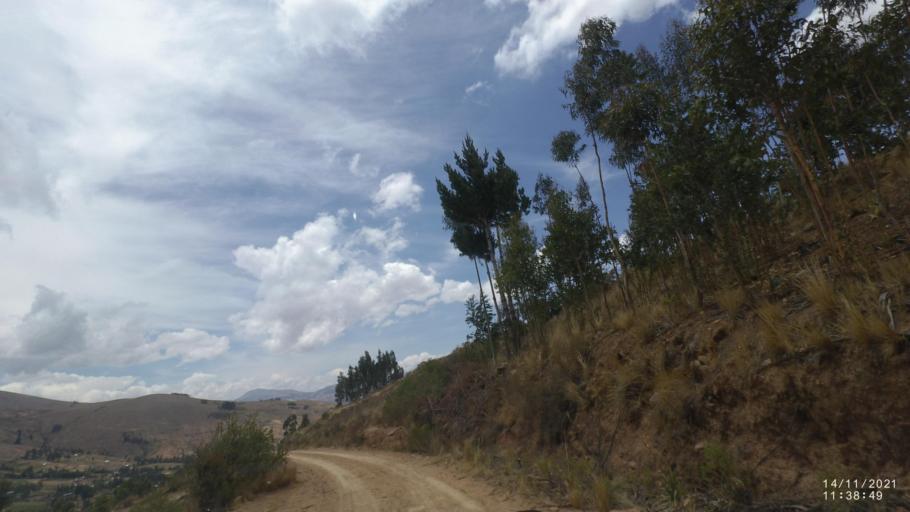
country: BO
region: Cochabamba
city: Colomi
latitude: -17.3479
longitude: -65.9971
